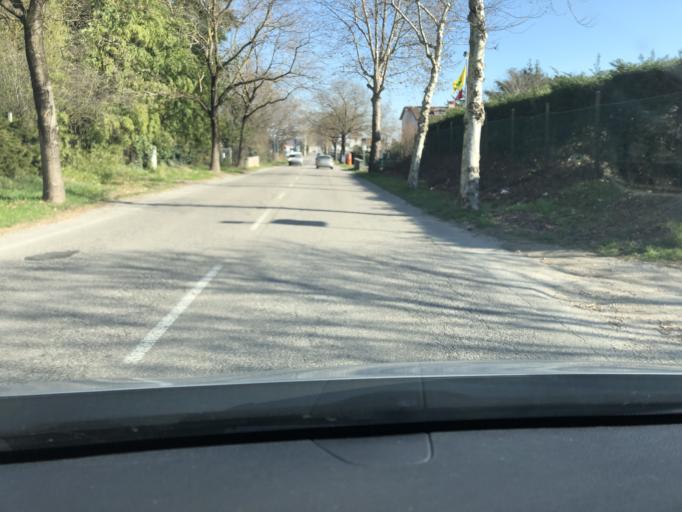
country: IT
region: Veneto
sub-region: Provincia di Verona
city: Bassone
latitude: 45.4467
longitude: 10.9189
